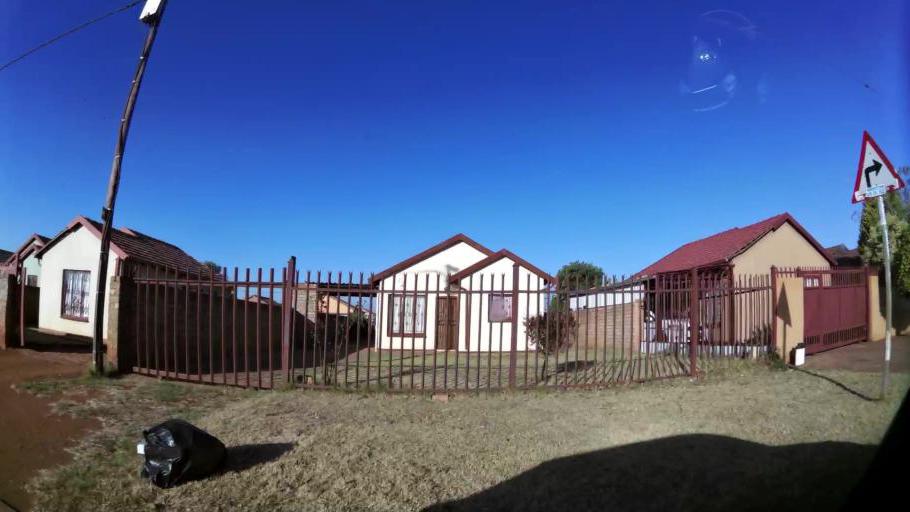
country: ZA
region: Gauteng
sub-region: City of Tshwane Metropolitan Municipality
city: Mabopane
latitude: -25.5969
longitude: 28.1114
